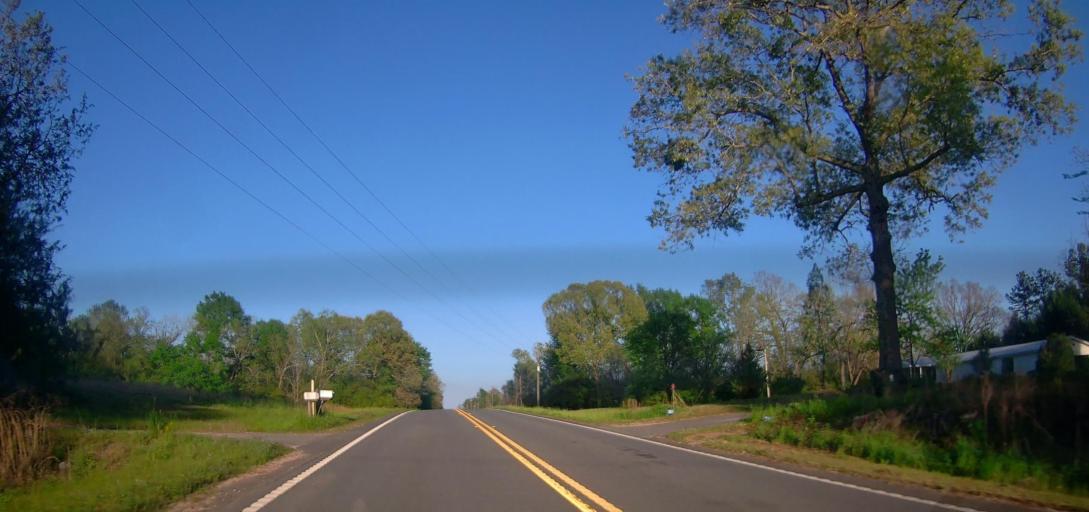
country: US
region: Georgia
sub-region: Schley County
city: Ellaville
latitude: 32.3211
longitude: -84.3002
